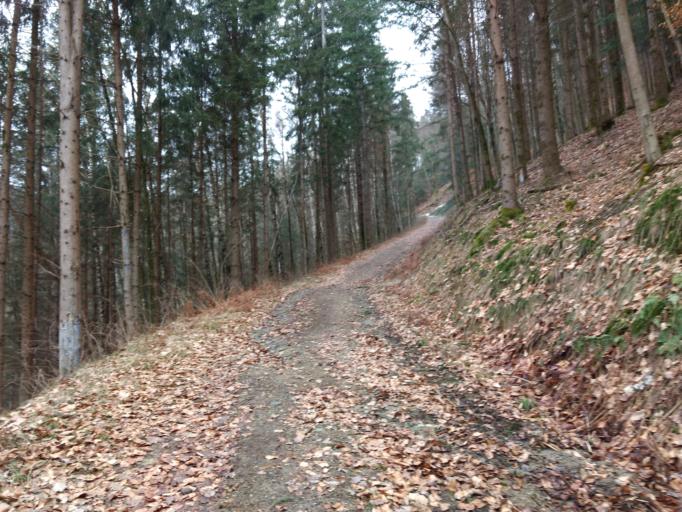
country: AT
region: Upper Austria
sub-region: Politischer Bezirk Rohrbach
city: Atzesberg
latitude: 48.4229
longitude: 13.8751
